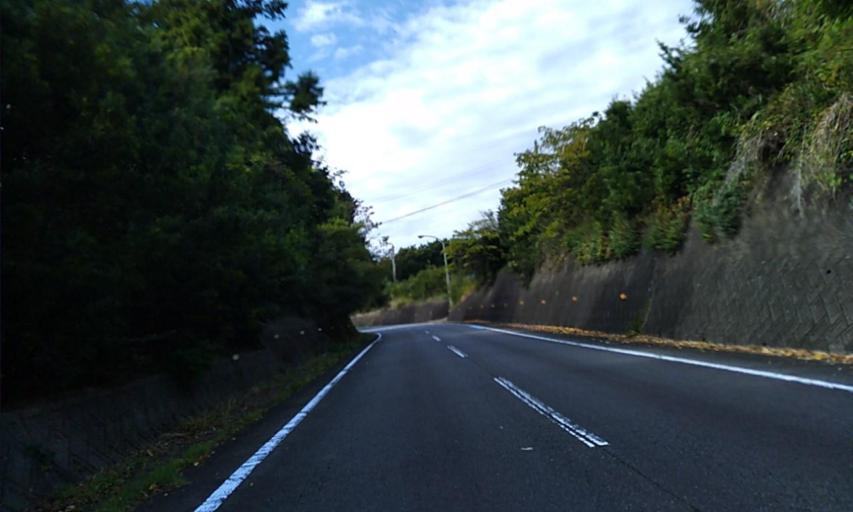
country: JP
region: Wakayama
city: Shingu
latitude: 33.4692
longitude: 135.8511
